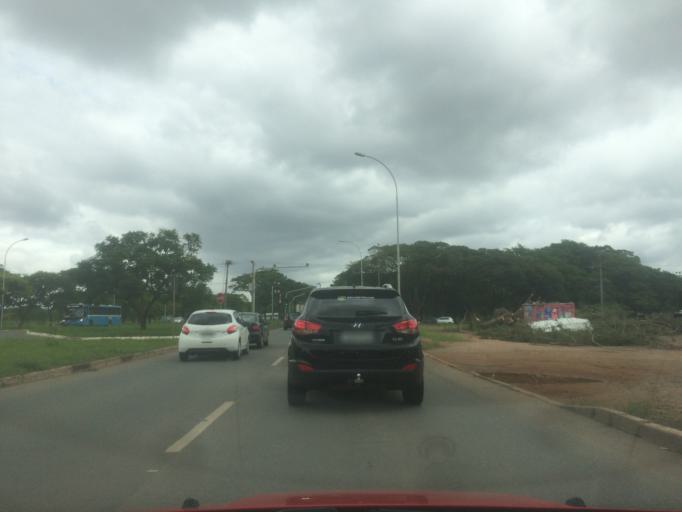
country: BR
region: Federal District
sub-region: Brasilia
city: Brasilia
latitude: -15.8410
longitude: -47.9212
